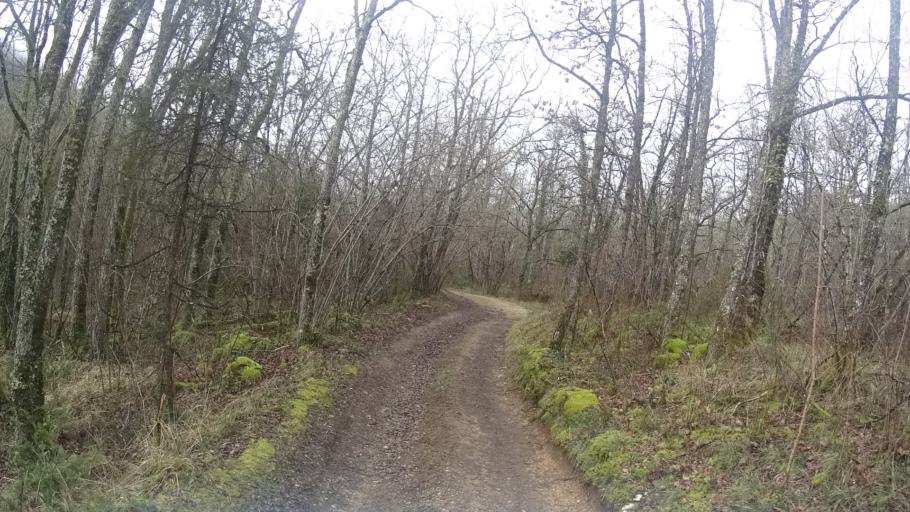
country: FR
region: Aquitaine
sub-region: Departement de la Dordogne
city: Terrasson-Lavilledieu
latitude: 45.1055
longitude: 1.2581
